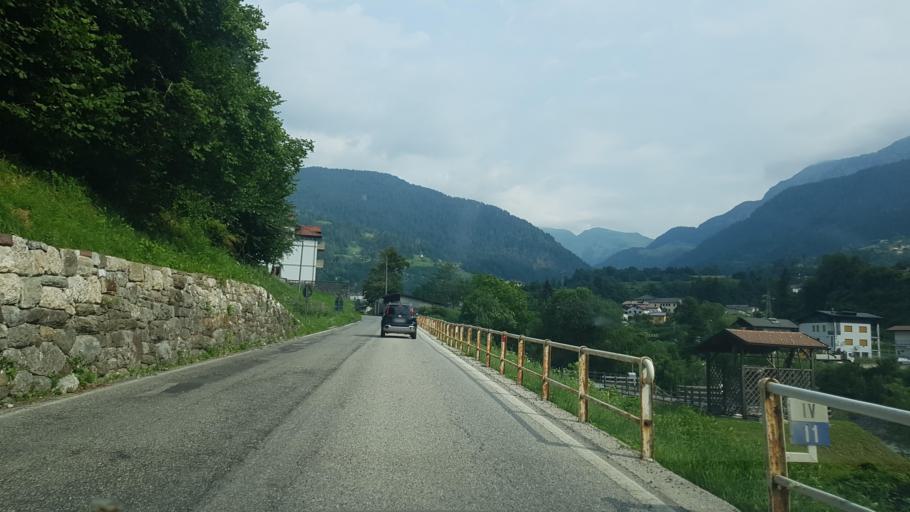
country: IT
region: Friuli Venezia Giulia
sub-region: Provincia di Udine
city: Paularo
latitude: 46.5244
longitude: 13.1211
